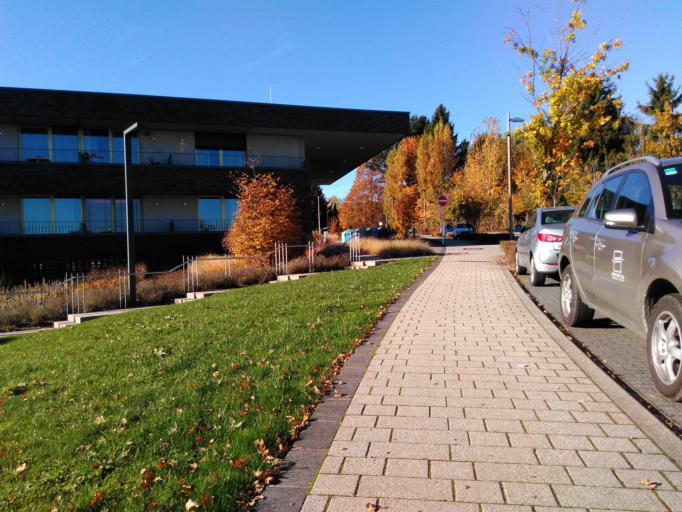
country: LU
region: Luxembourg
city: Belvaux
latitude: 49.5090
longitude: 5.9339
